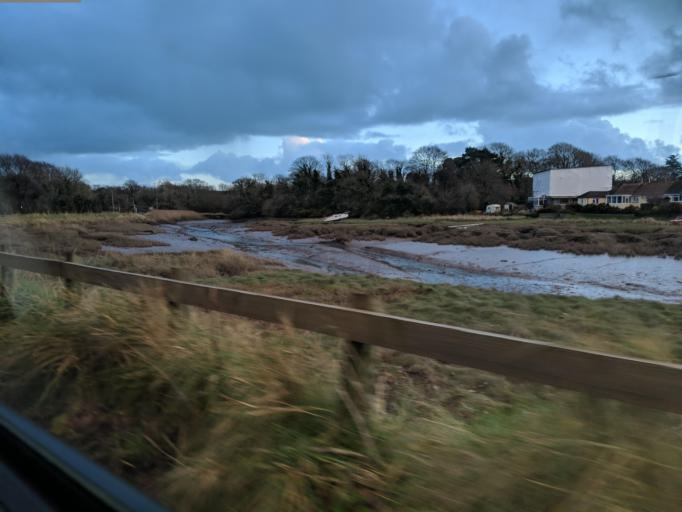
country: GB
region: England
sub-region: Devon
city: Fremington
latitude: 51.0744
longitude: -4.1160
